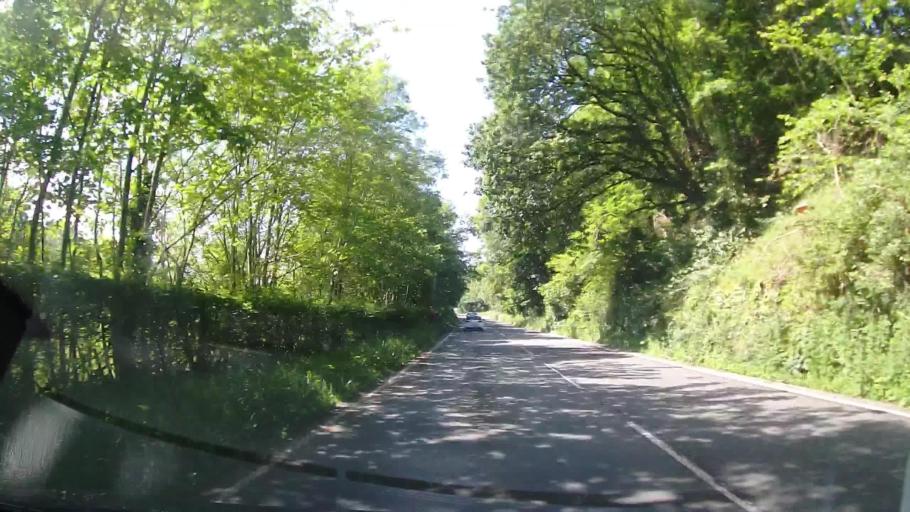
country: GB
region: Wales
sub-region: Sir Powys
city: Machynlleth
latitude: 52.5680
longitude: -3.9552
